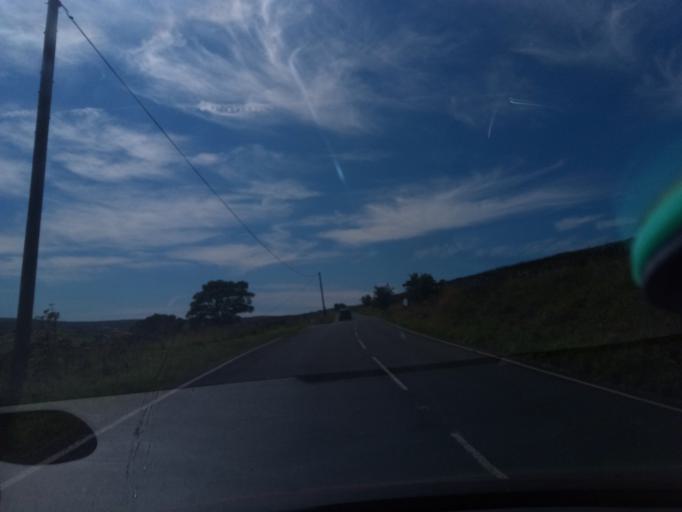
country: GB
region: England
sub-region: Northumberland
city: Bardon Mill
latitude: 54.8731
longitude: -2.3543
